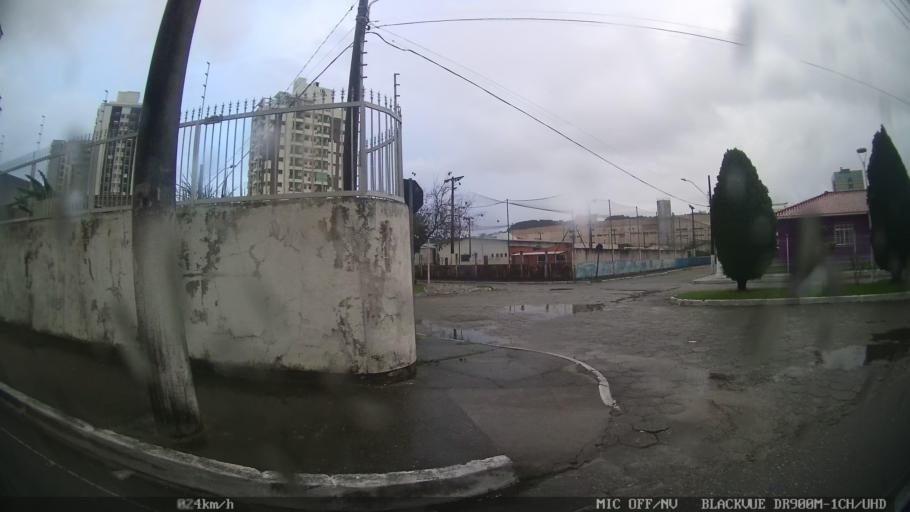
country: BR
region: Santa Catarina
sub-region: Sao Jose
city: Campinas
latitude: -27.6001
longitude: -48.6181
